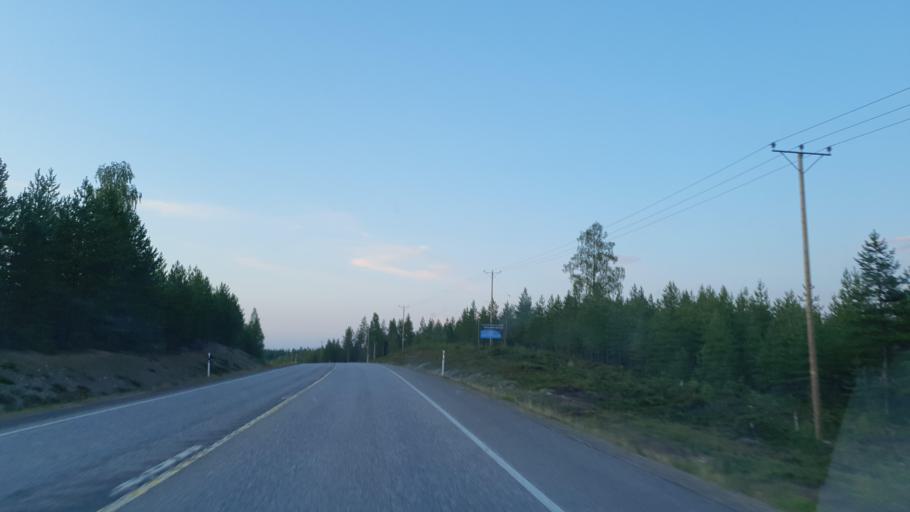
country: FI
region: Kainuu
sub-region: Kehys-Kainuu
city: Suomussalmi
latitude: 64.8423
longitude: 28.9554
